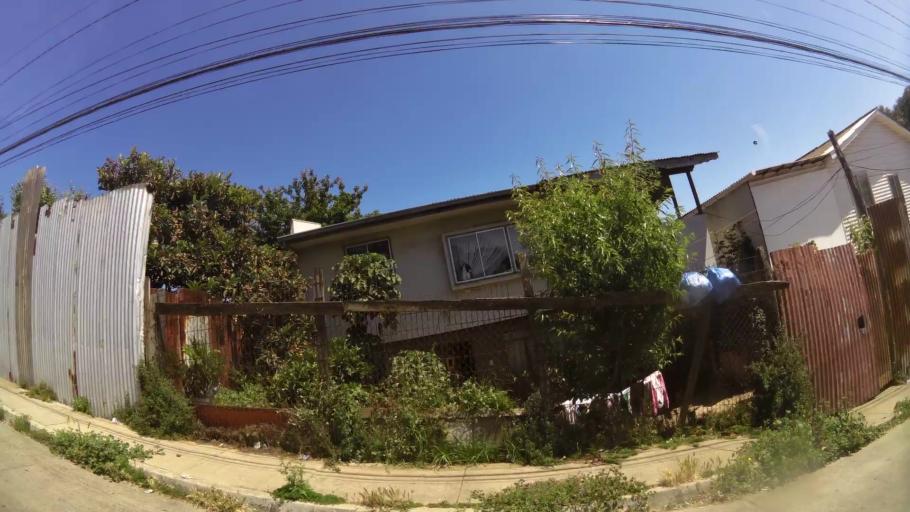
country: CL
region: Valparaiso
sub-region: Provincia de Valparaiso
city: Valparaiso
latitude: -33.0335
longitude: -71.6507
